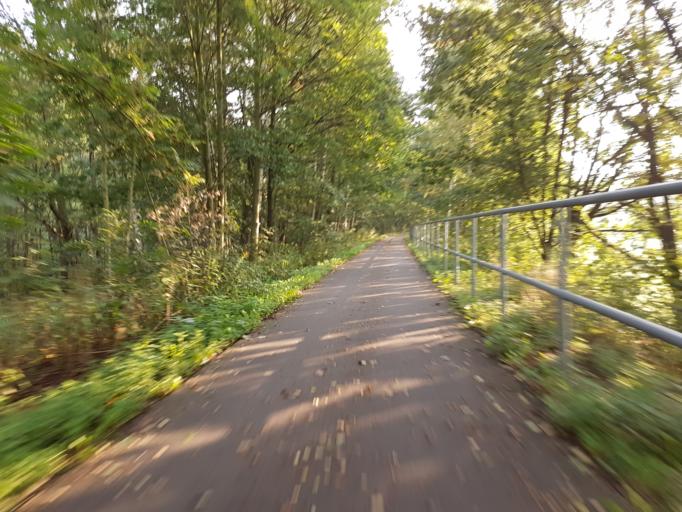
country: DE
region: Saxony
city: Claussnitz
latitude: 50.9162
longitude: 12.8719
